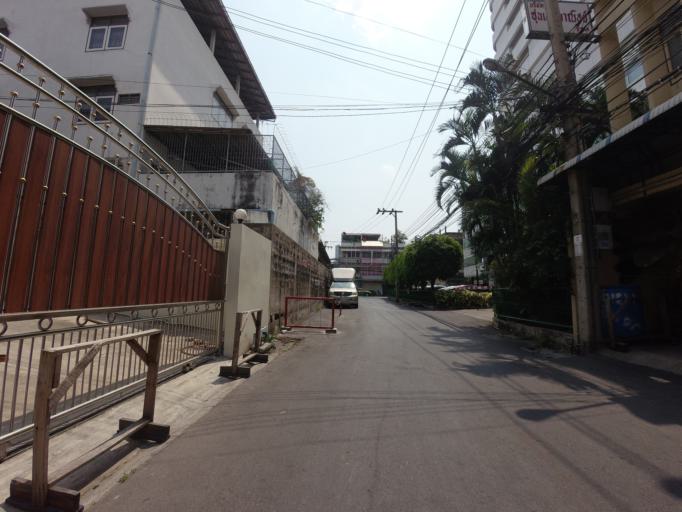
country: TH
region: Bangkok
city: Din Daeng
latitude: 13.7616
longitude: 100.5592
